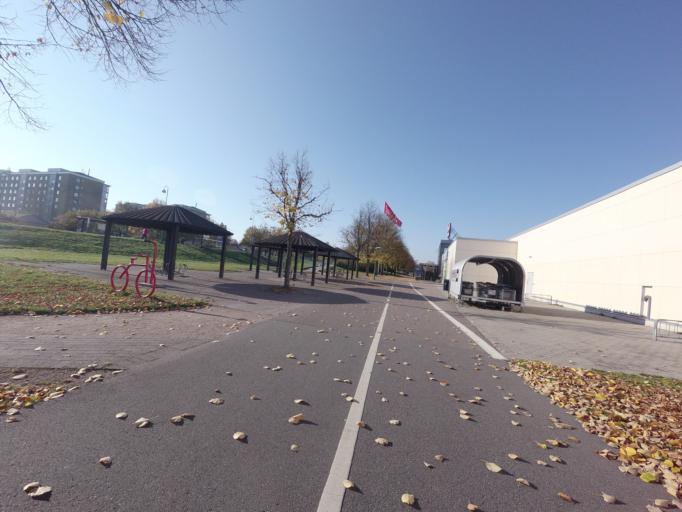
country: SE
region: Skane
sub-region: Burlovs Kommun
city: Arloev
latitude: 55.6393
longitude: 13.0860
